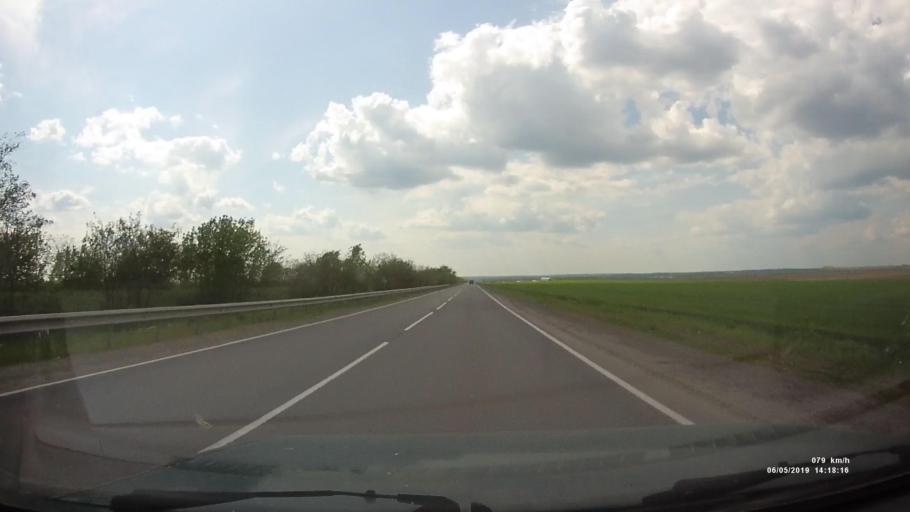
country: RU
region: Rostov
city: Kamenolomni
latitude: 47.6336
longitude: 40.2529
